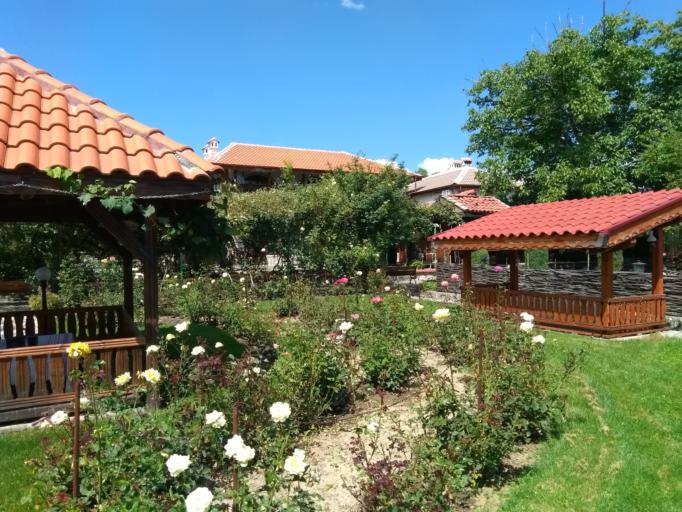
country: BG
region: Stara Zagora
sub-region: Obshtina Pavel Banya
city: Asen
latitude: 42.6691
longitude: 25.2016
